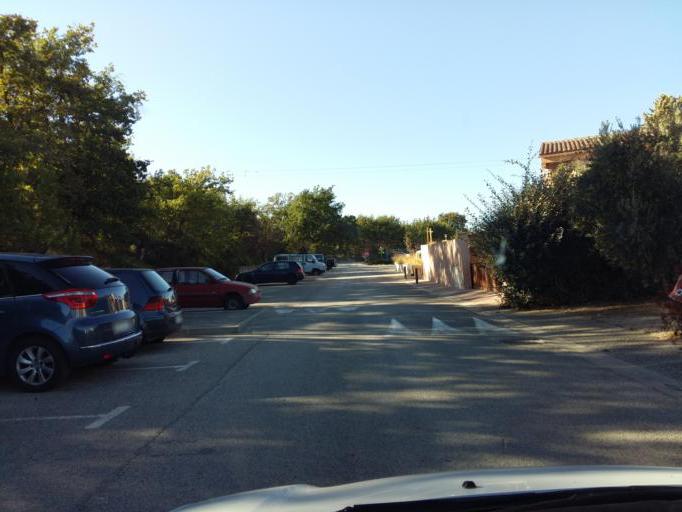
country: FR
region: Provence-Alpes-Cote d'Azur
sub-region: Departement du Vaucluse
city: Pertuis
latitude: 43.7209
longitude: 5.5371
